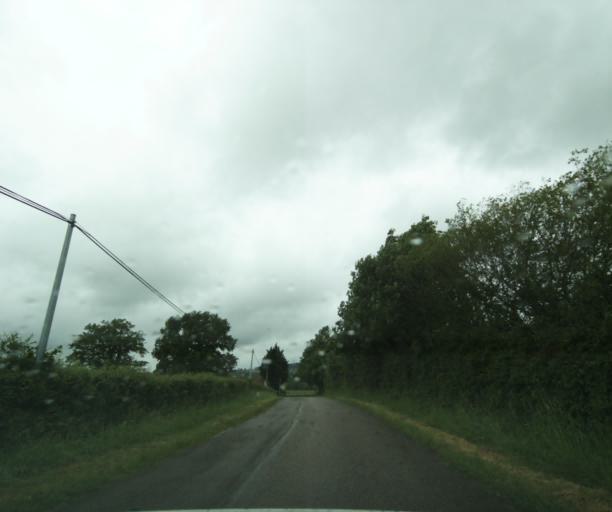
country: FR
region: Bourgogne
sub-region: Departement de Saone-et-Loire
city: Charolles
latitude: 46.4645
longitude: 4.4378
